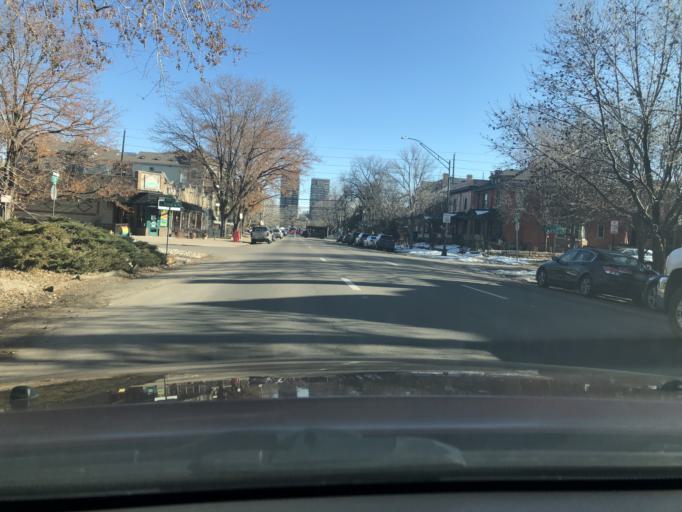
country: US
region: Colorado
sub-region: Denver County
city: Denver
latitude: 39.7433
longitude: -104.9627
